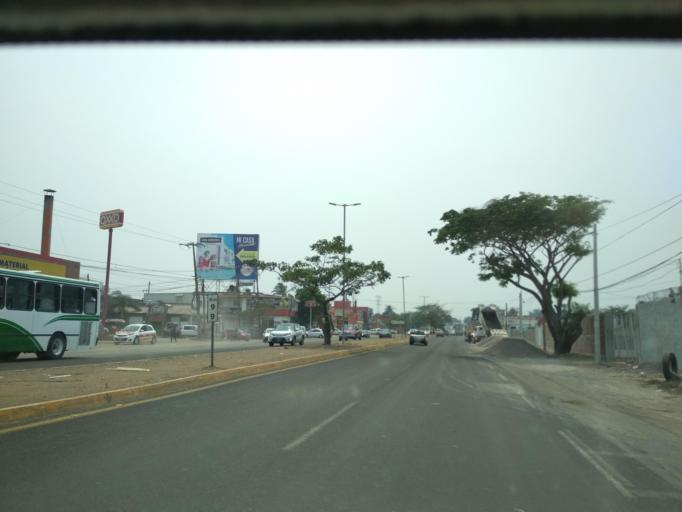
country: MX
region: Veracruz
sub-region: Veracruz
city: Las Amapolas
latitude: 19.1625
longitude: -96.2073
